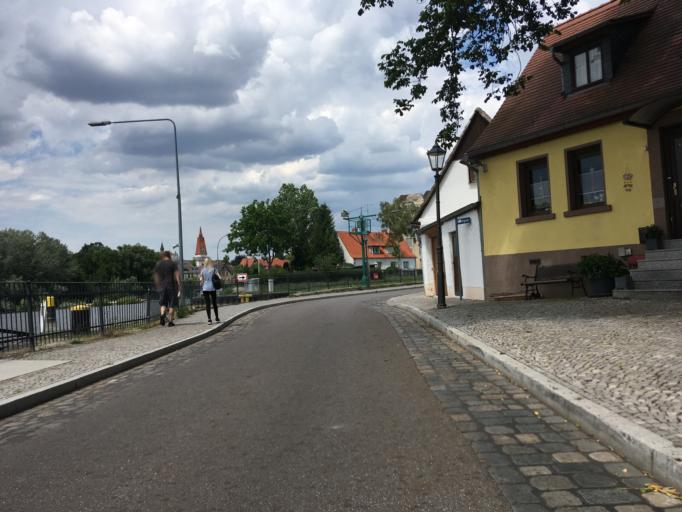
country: DE
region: Saxony-Anhalt
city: Bernburg
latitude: 51.7949
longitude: 11.7335
